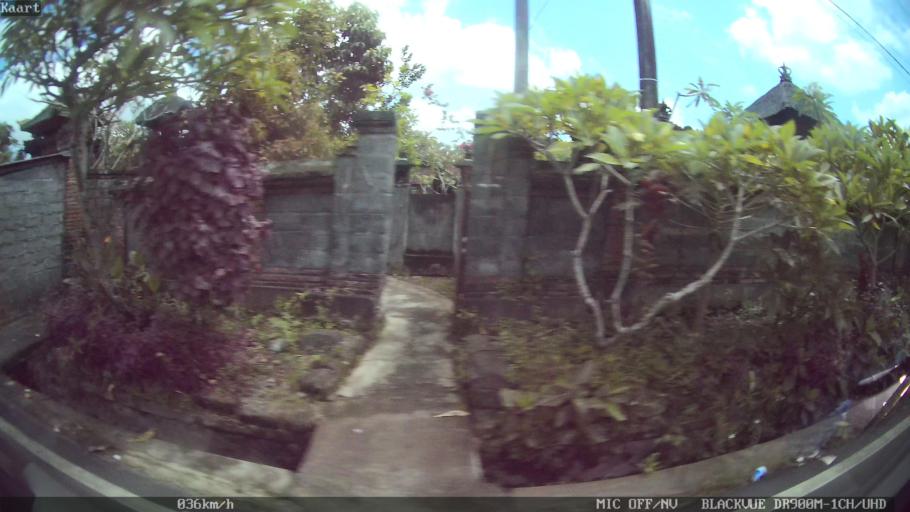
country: ID
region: Bali
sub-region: Kabupaten Gianyar
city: Ubud
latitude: -8.5341
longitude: 115.2821
